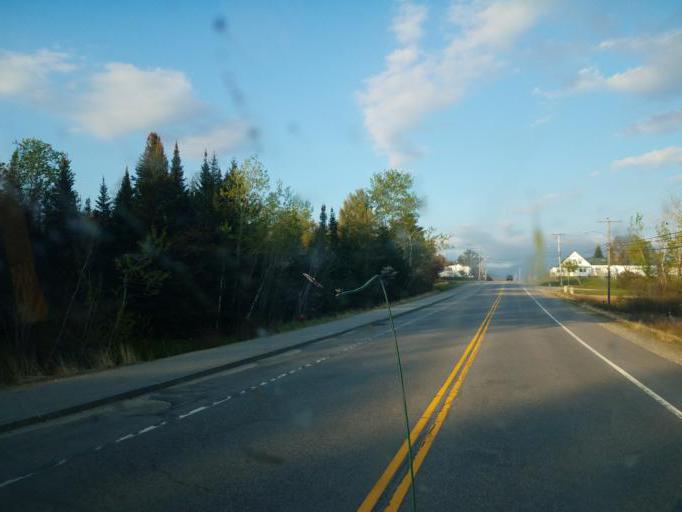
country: US
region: New Hampshire
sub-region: Grafton County
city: Deerfield
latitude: 44.2675
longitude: -71.5551
